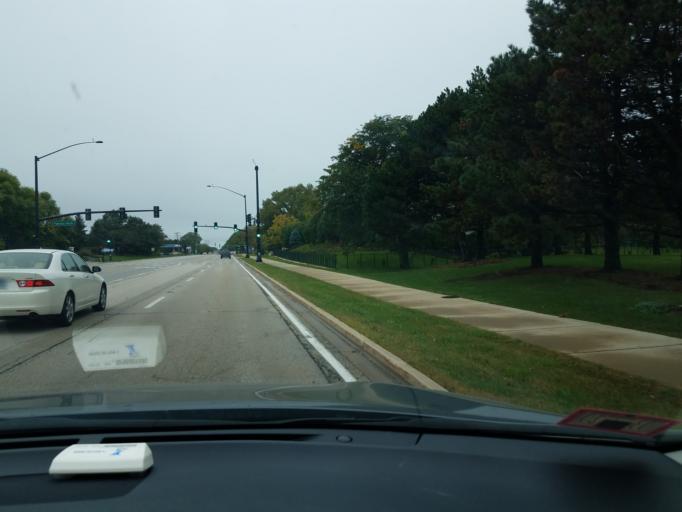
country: US
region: Illinois
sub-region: Lake County
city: Riverwoods
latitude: 42.1676
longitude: -87.8786
